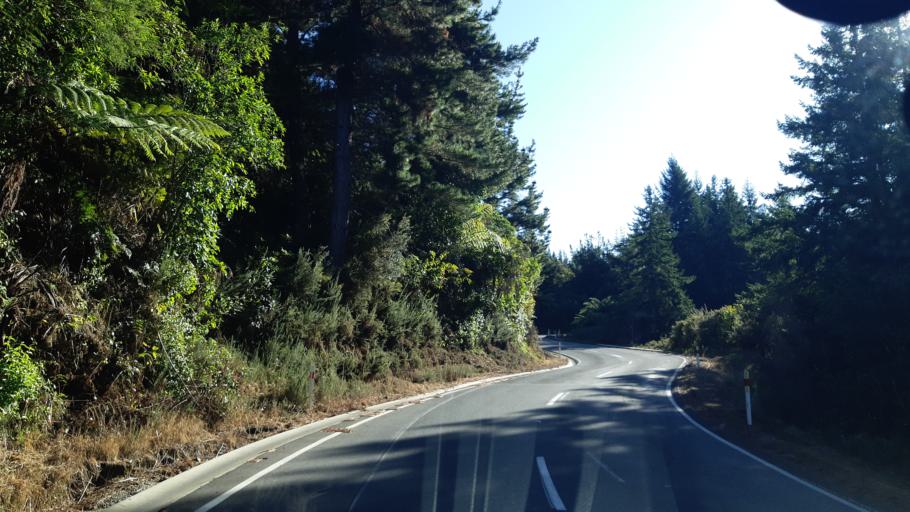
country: NZ
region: Tasman
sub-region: Tasman District
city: Motueka
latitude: -41.0482
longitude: 172.9788
